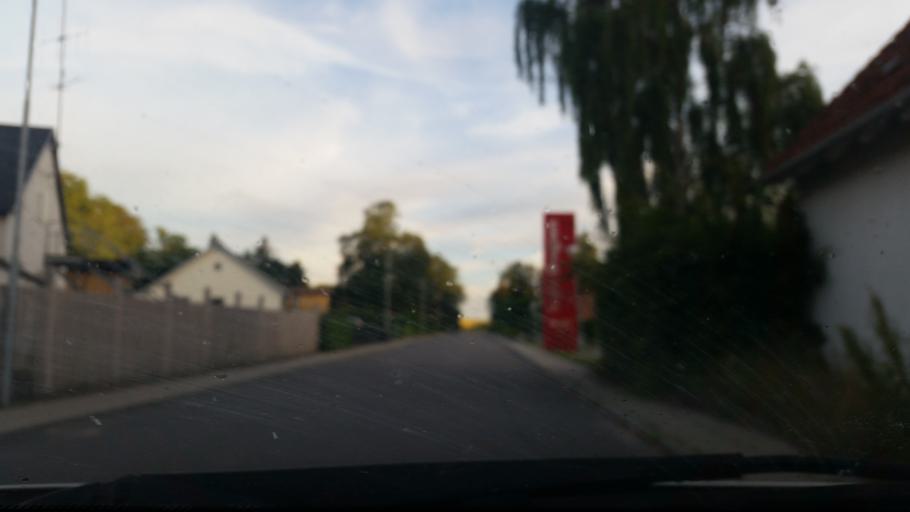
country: DK
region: Central Jutland
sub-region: Samso Kommune
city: Tranebjerg
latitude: 55.8314
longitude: 10.5942
